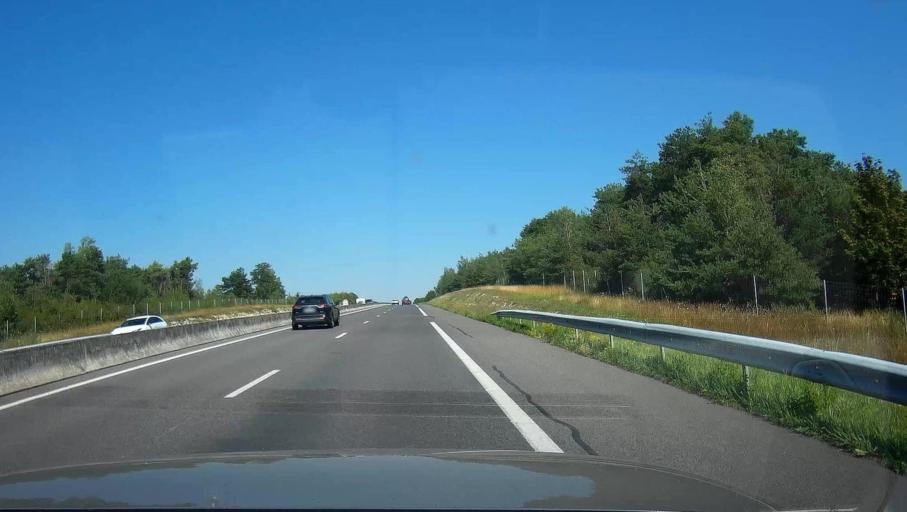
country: FR
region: Champagne-Ardenne
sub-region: Departement de l'Aube
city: Arcis-sur-Aube
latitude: 48.4862
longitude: 4.1653
